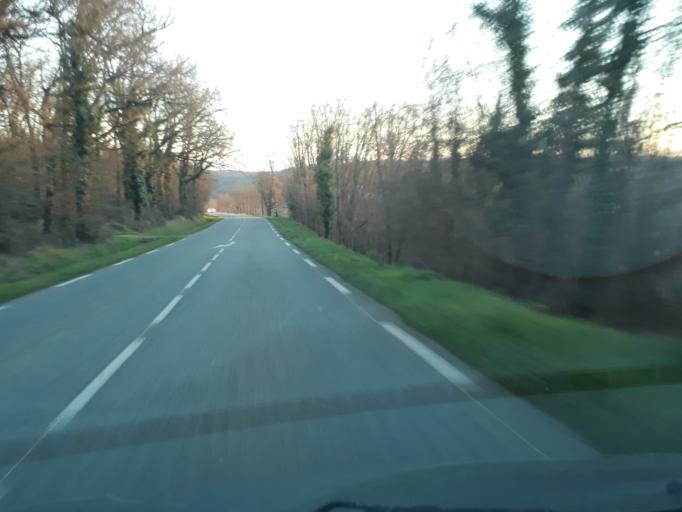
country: FR
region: Midi-Pyrenees
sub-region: Departement du Gers
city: Pujaudran
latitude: 43.5756
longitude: 1.1288
